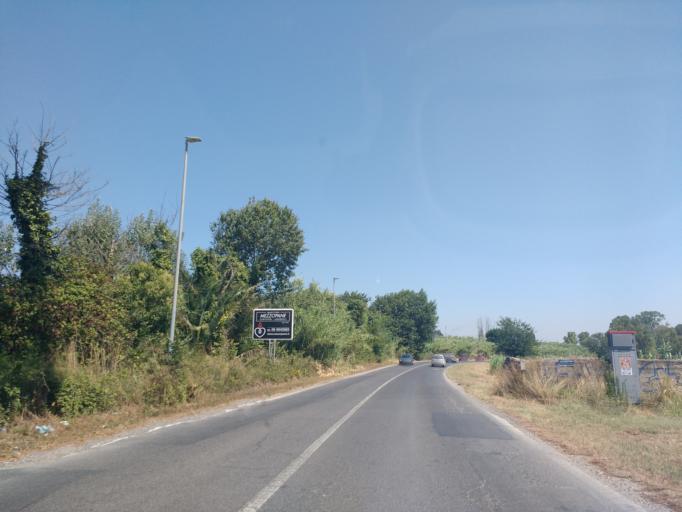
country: IT
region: Latium
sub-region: Citta metropolitana di Roma Capitale
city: Maccarese
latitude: 41.8728
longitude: 12.2091
